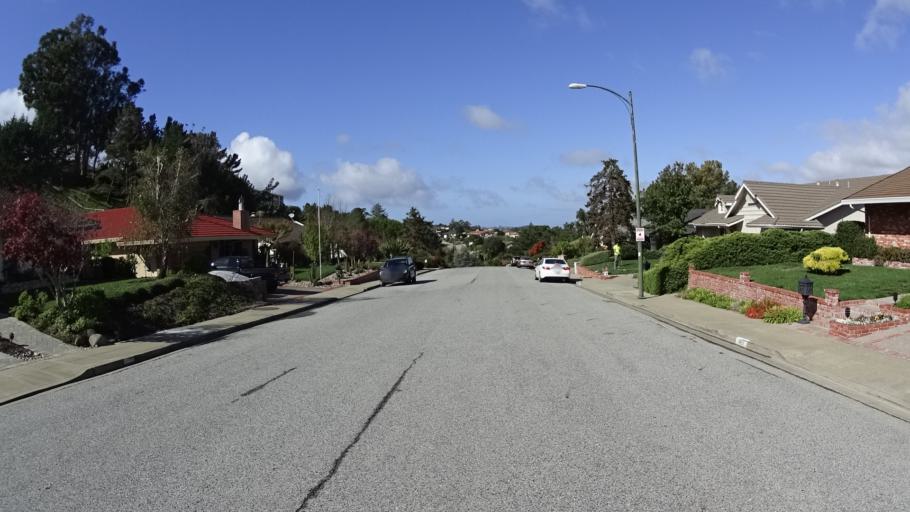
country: US
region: California
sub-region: San Mateo County
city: Millbrae
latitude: 37.5839
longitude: -122.4025
